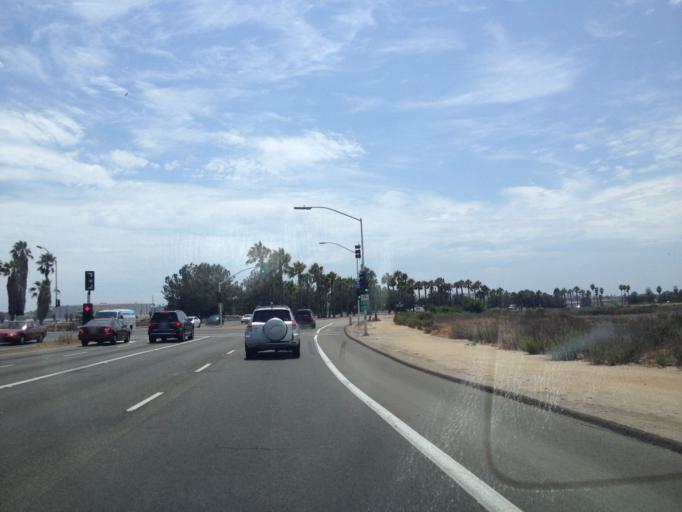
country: US
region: California
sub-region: San Diego County
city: San Diego
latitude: 32.7642
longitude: -117.2092
